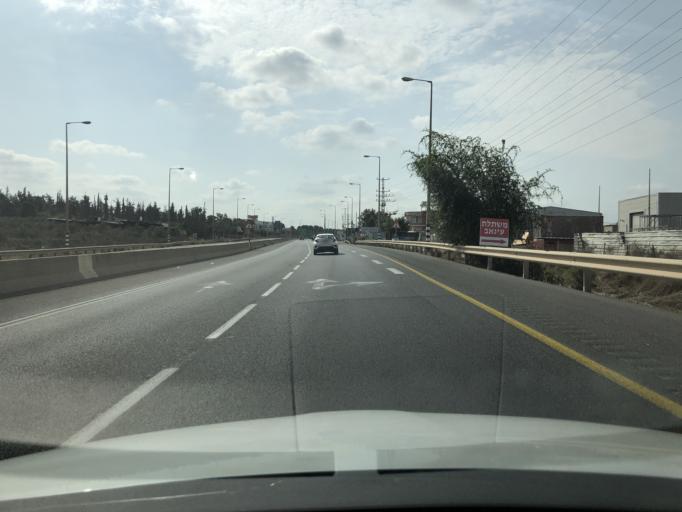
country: IL
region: Central District
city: Tirah
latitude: 32.2250
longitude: 34.9813
